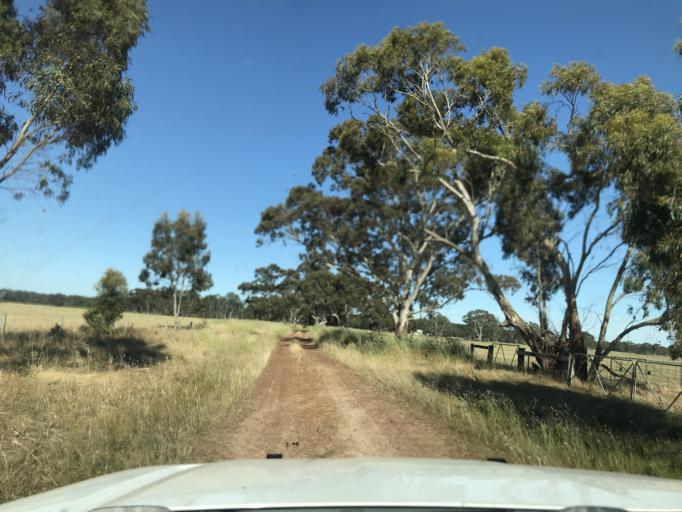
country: AU
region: South Australia
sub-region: Wattle Range
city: Penola
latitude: -37.0803
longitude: 141.3826
